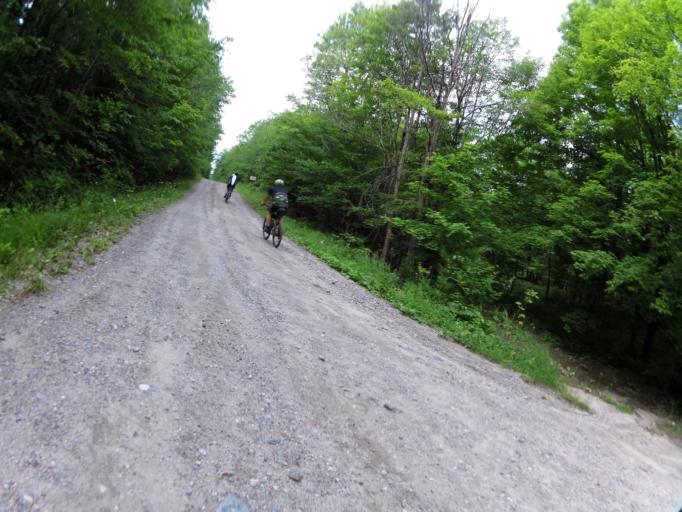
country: CA
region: Ontario
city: Perth
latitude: 45.0289
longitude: -76.5674
